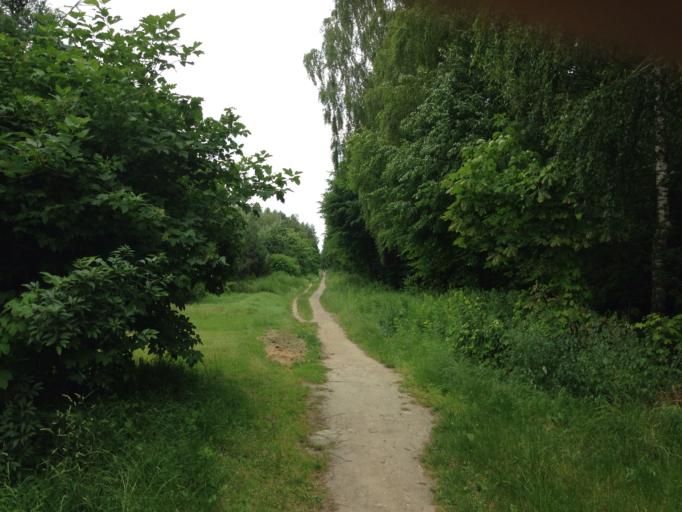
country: PL
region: Masovian Voivodeship
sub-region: Powiat warszawski zachodni
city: Babice
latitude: 52.2501
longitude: 20.8639
